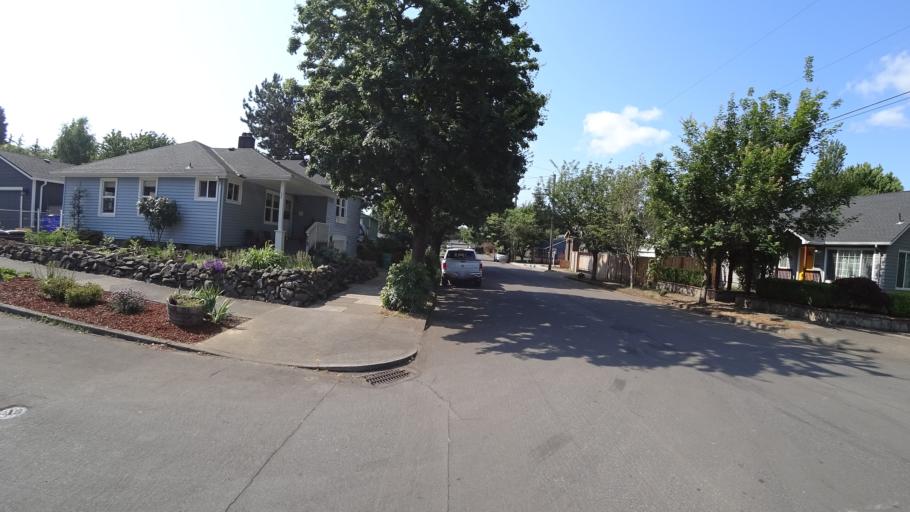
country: US
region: Washington
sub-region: Clark County
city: Vancouver
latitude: 45.5984
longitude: -122.7348
